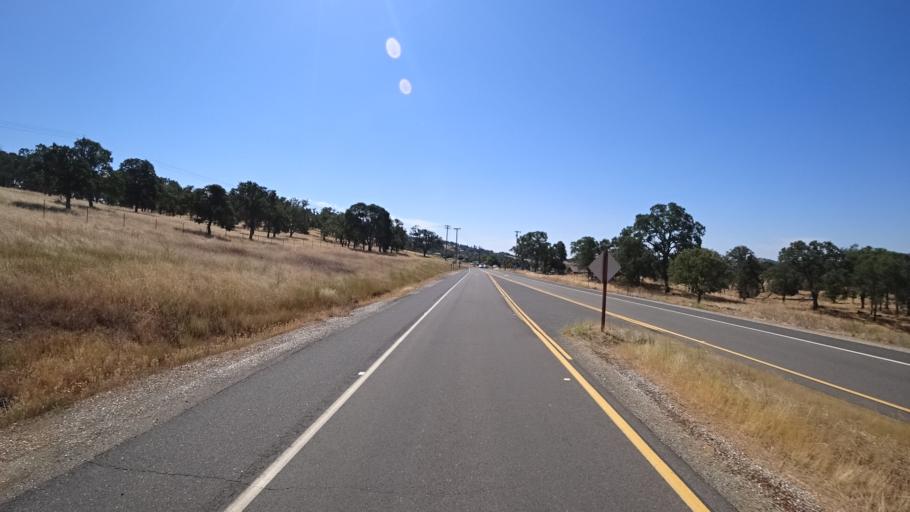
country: US
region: California
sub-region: Calaveras County
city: Copperopolis
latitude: 37.9390
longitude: -120.6458
